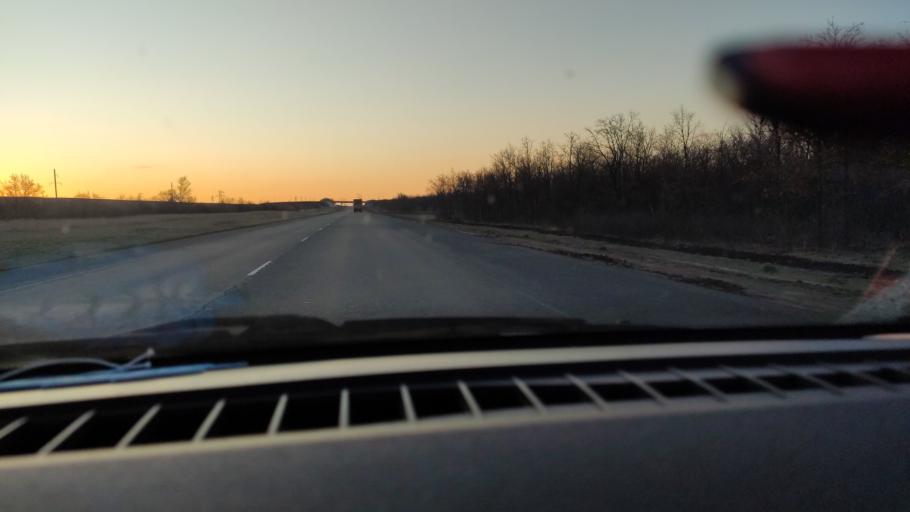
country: RU
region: Saratov
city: Yelshanka
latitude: 51.8266
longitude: 46.2789
